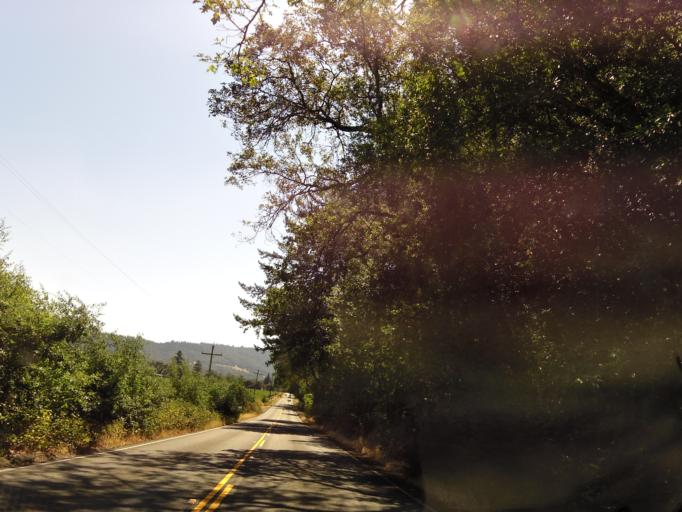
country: US
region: California
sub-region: Sonoma County
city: Cloverdale
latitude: 38.8250
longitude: -123.0333
